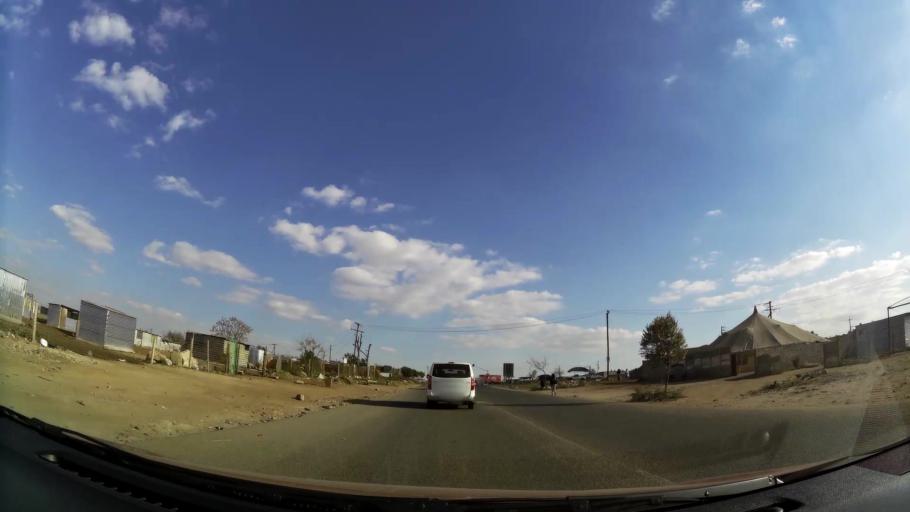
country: ZA
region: Gauteng
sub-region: Ekurhuleni Metropolitan Municipality
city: Tembisa
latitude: -25.9957
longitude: 28.1876
